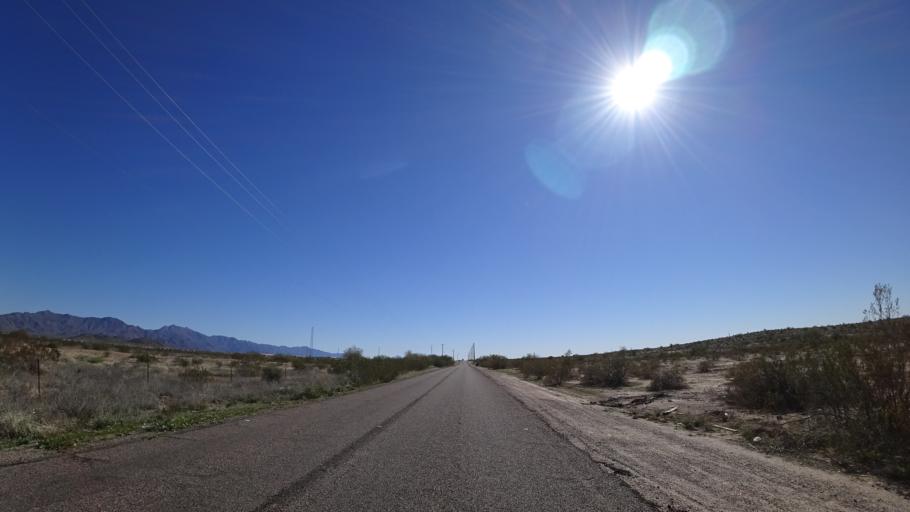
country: US
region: Arizona
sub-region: Maricopa County
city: Buckeye
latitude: 33.2970
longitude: -112.4535
